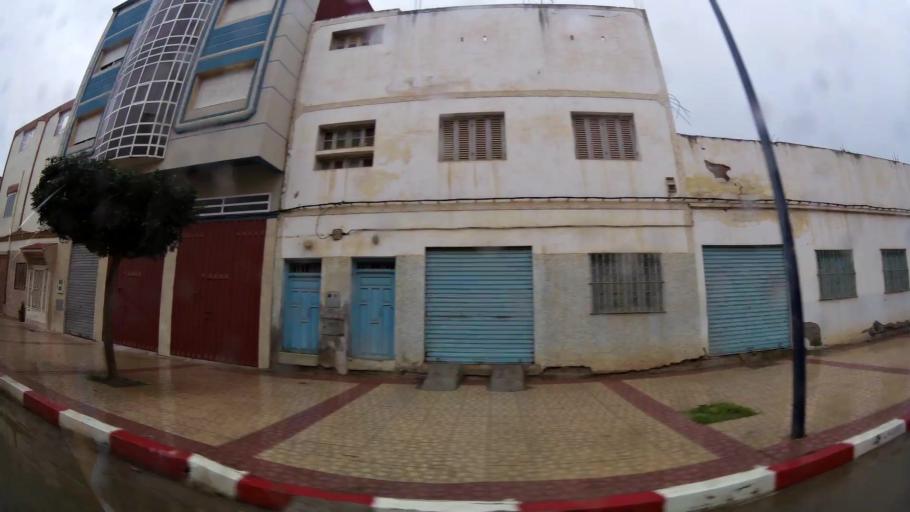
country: MA
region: Taza-Al Hoceima-Taounate
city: Imzourene
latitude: 35.1387
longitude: -3.8524
